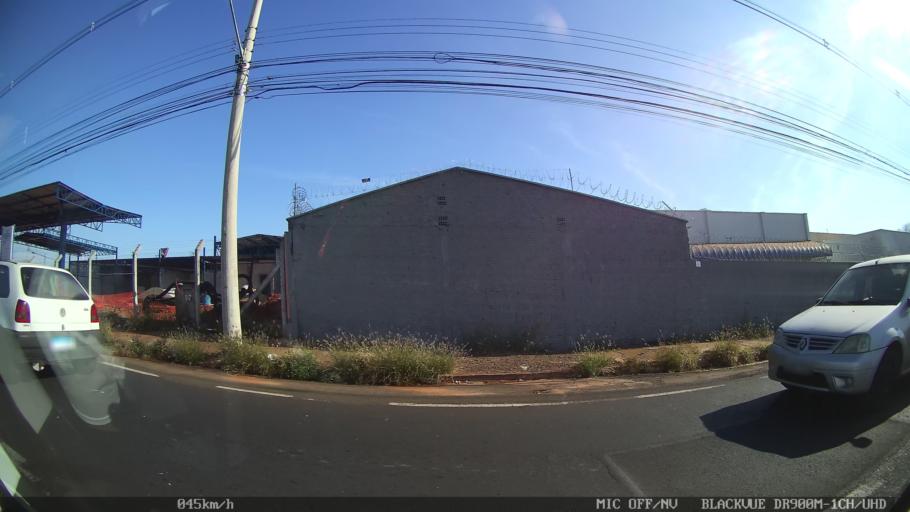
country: BR
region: Sao Paulo
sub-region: Sao Jose Do Rio Preto
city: Sao Jose do Rio Preto
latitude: -20.7791
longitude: -49.4033
